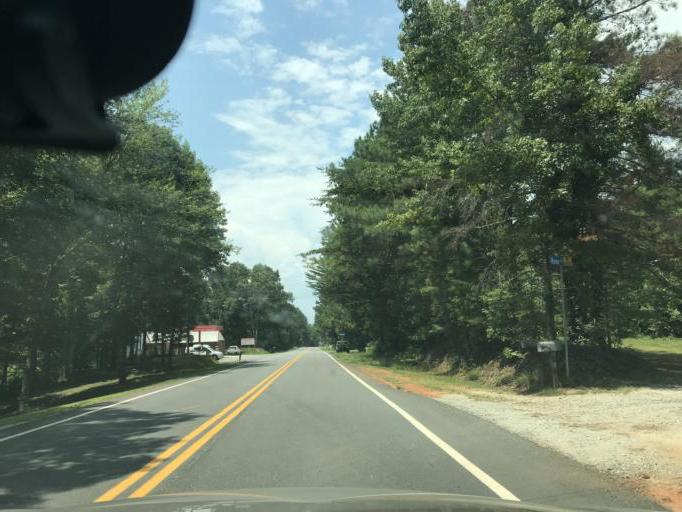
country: US
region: Georgia
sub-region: Dawson County
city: Dawsonville
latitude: 34.3403
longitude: -84.1643
